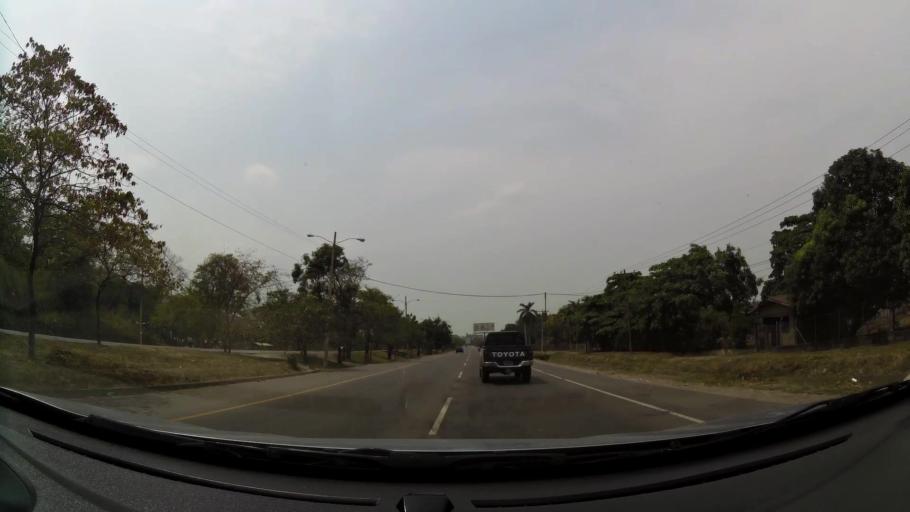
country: HN
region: Cortes
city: Nuevo Chamelecon
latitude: 15.3861
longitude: -87.9907
